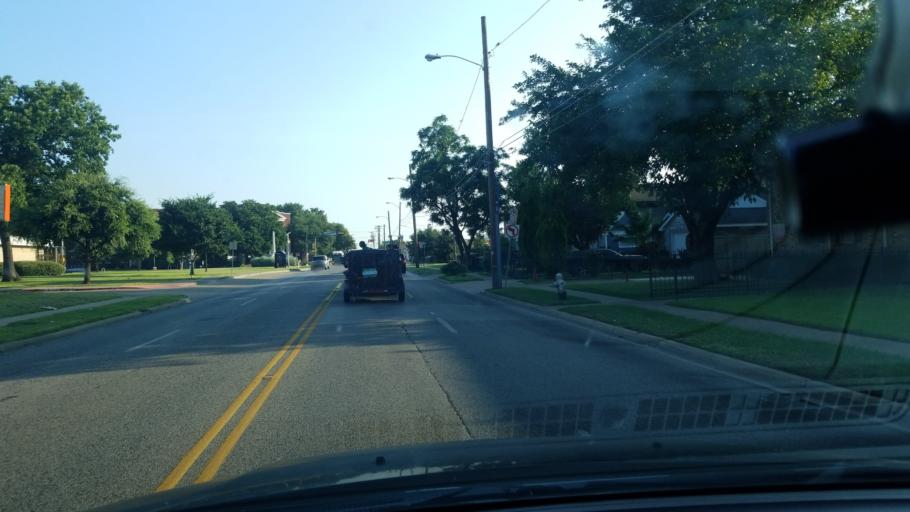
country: US
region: Texas
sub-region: Dallas County
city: Dallas
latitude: 32.7460
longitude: -96.8156
